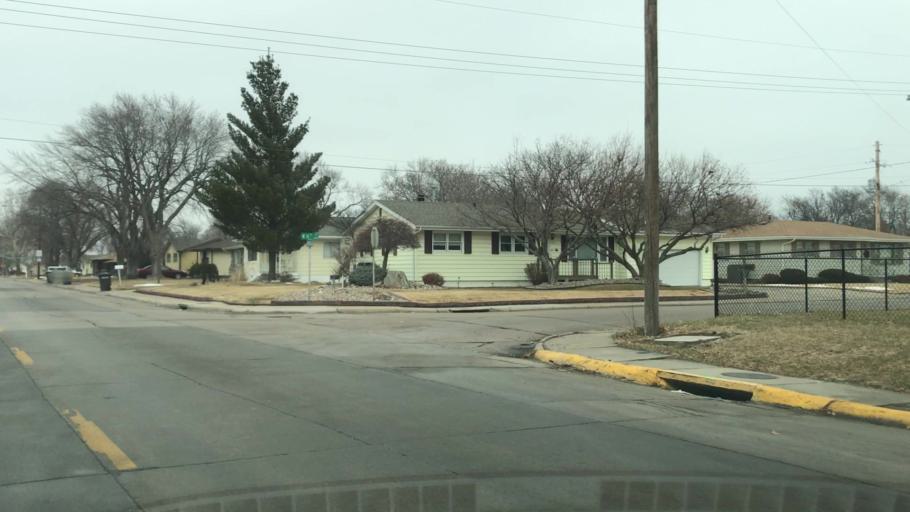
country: US
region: Nebraska
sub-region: Hall County
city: Grand Island
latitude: 40.9349
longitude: -98.3685
